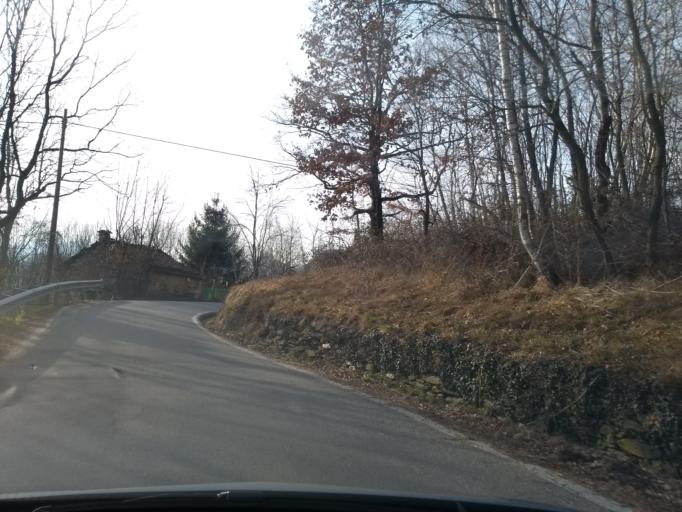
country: IT
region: Piedmont
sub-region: Provincia di Torino
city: Lanzo Torinese
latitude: 45.2890
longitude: 7.5023
